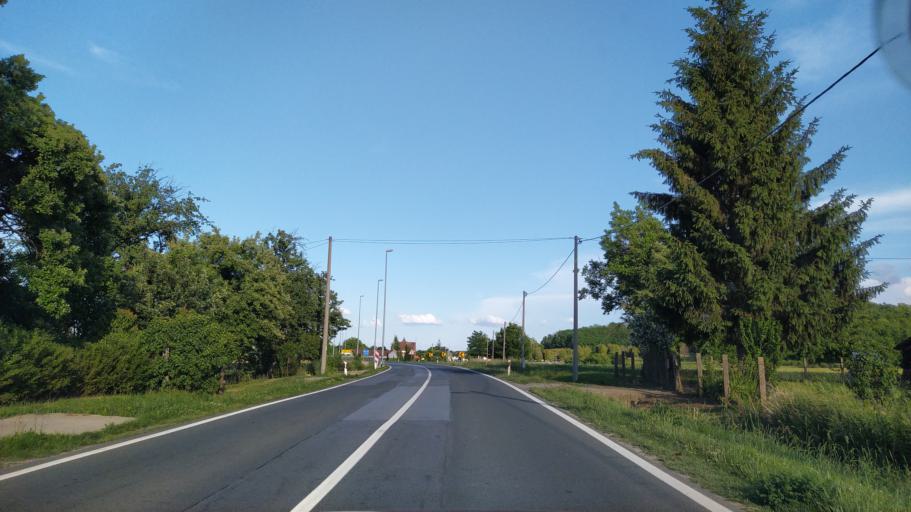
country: HR
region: Virovitick-Podravska
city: Slatina
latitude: 45.7255
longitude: 17.6366
